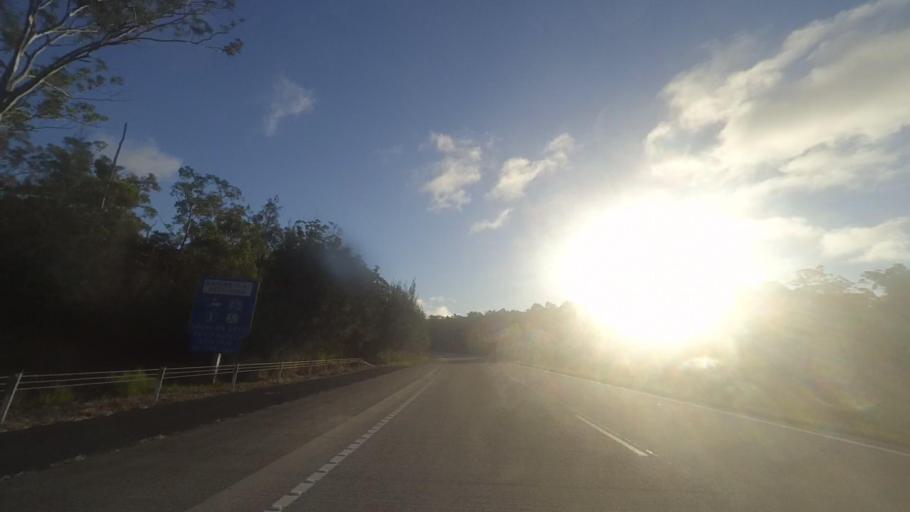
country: AU
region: New South Wales
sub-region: Great Lakes
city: Hawks Nest
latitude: -32.5495
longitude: 152.1534
